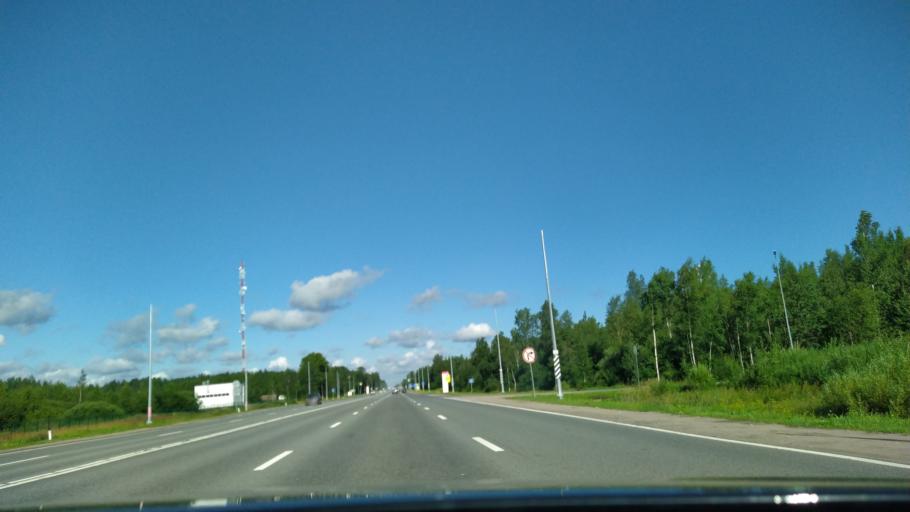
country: RU
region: Leningrad
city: Tosno
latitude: 59.5695
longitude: 30.8251
